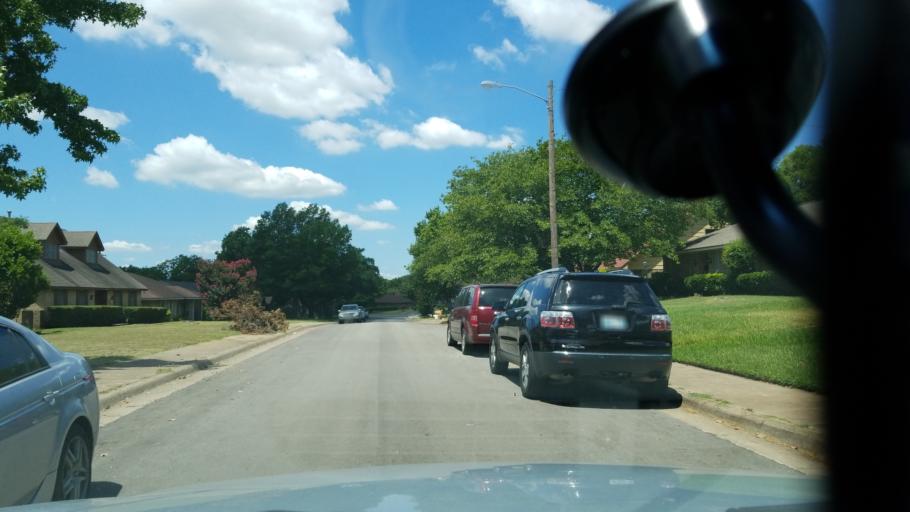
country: US
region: Texas
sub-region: Dallas County
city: Duncanville
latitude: 32.6691
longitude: -96.8607
